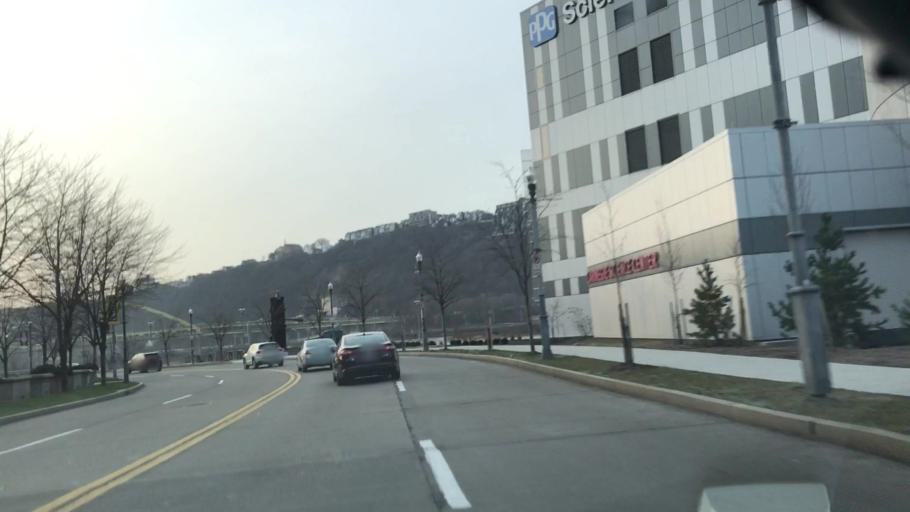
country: US
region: Pennsylvania
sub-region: Allegheny County
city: Pittsburgh
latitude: 40.4460
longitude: -80.0172
